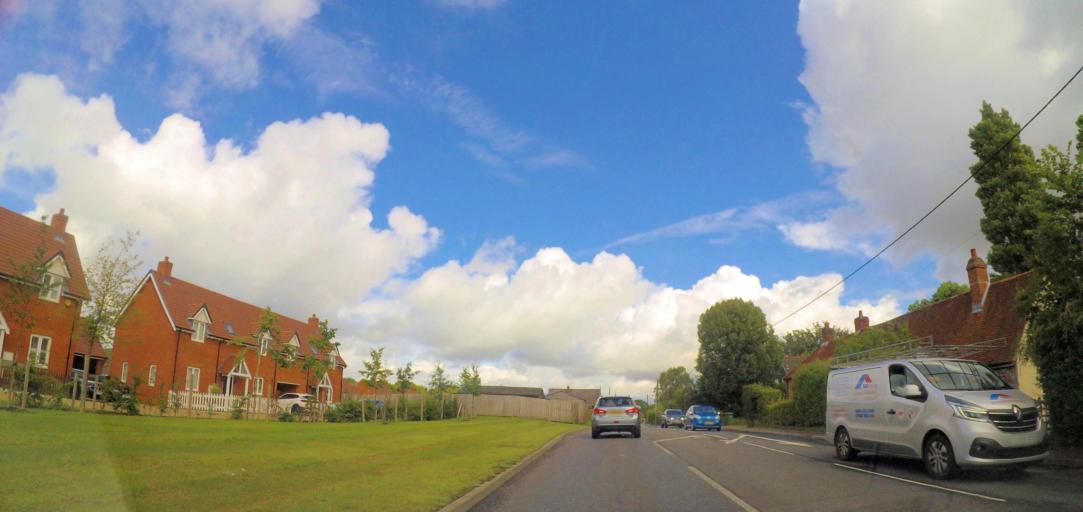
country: GB
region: England
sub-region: Hampshire
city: Colden Common
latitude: 50.9739
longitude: -1.3021
